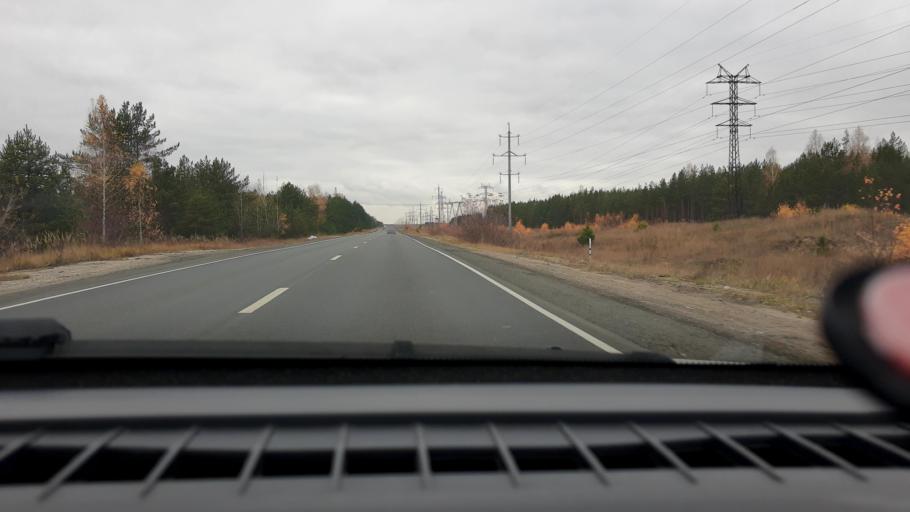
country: RU
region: Nizjnij Novgorod
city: Lukino
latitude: 56.3939
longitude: 43.6455
